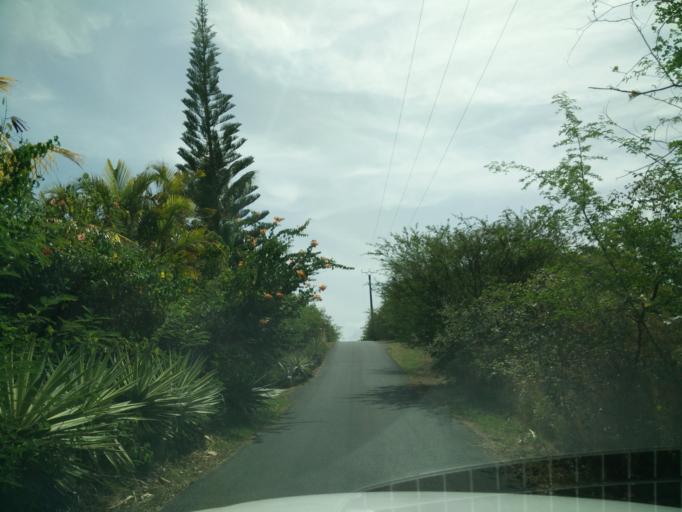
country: GP
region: Guadeloupe
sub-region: Guadeloupe
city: Sainte-Anne
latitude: 16.2434
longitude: -61.3386
